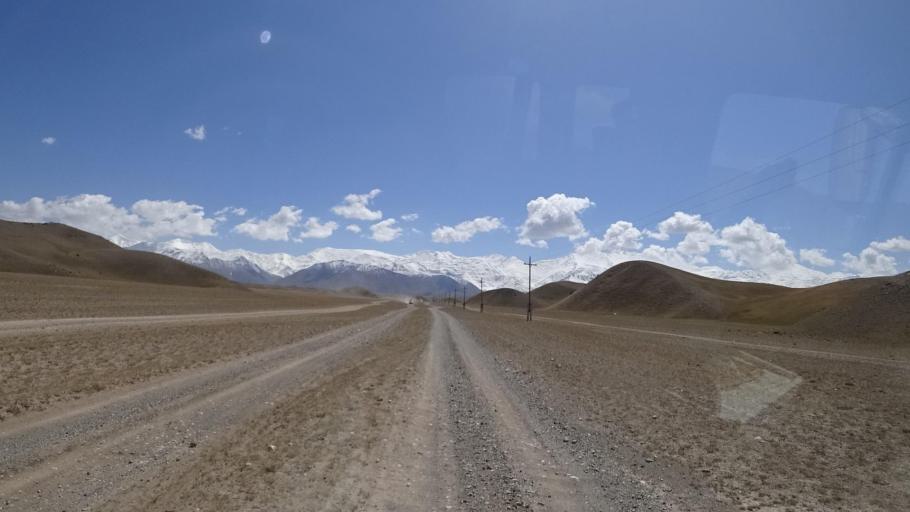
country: KG
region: Osh
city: Gul'cha
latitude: 39.5988
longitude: 72.8826
